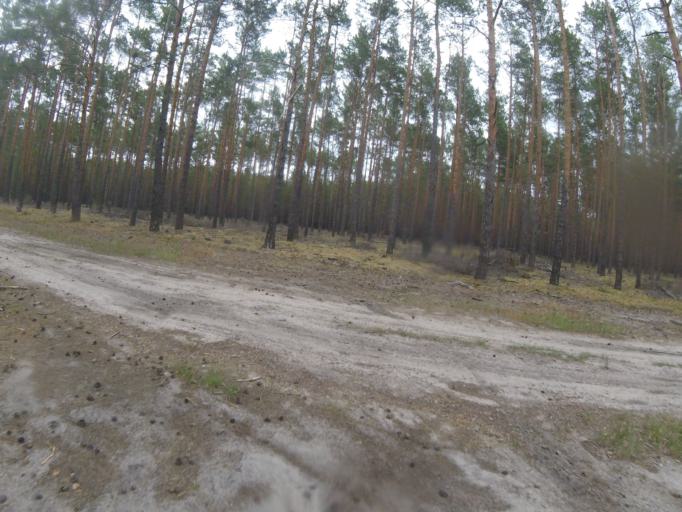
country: DE
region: Brandenburg
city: Gross Koris
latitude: 52.1910
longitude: 13.6601
